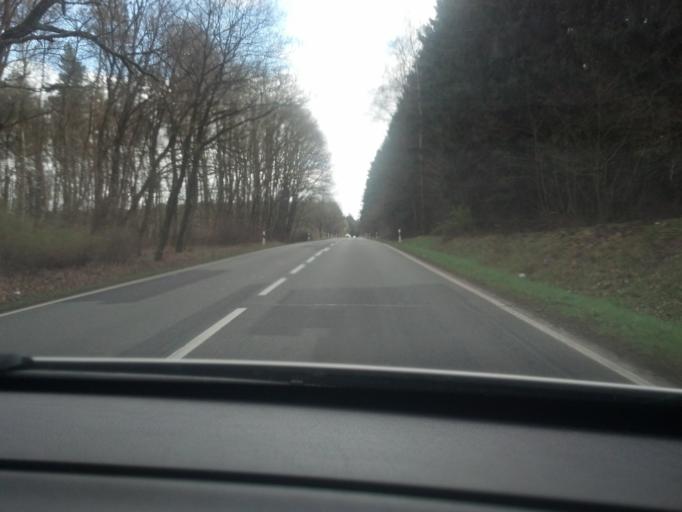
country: DE
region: Mecklenburg-Vorpommern
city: Plau am See
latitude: 53.3840
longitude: 12.3142
